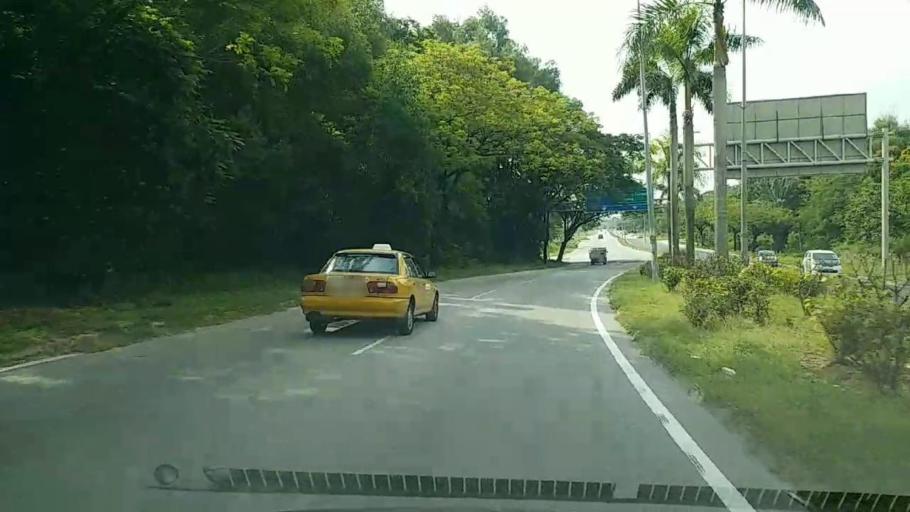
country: MY
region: Putrajaya
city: Putrajaya
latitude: 2.9664
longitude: 101.6146
